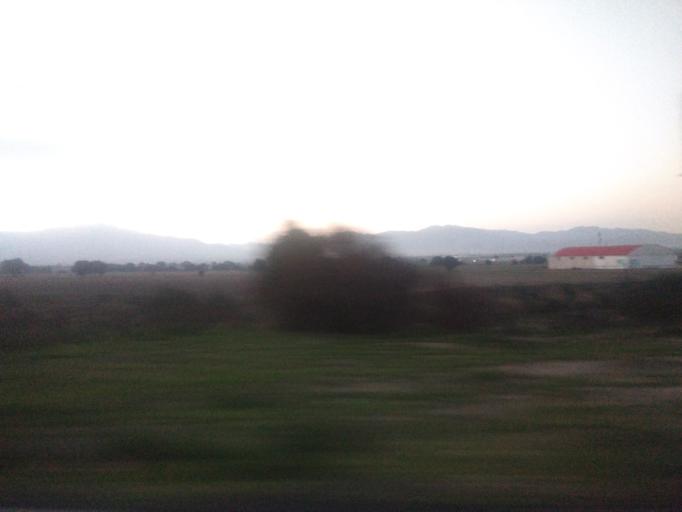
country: MX
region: Puebla
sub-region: Oriental
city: San Antonio Virreyes
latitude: 19.4152
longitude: -97.6450
